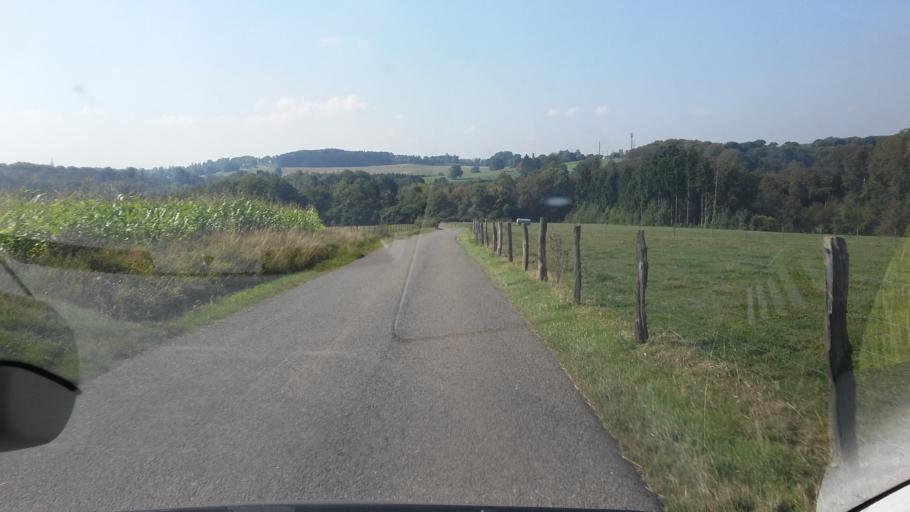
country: BE
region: Wallonia
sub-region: Province du Luxembourg
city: Arlon
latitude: 49.7142
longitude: 5.8430
